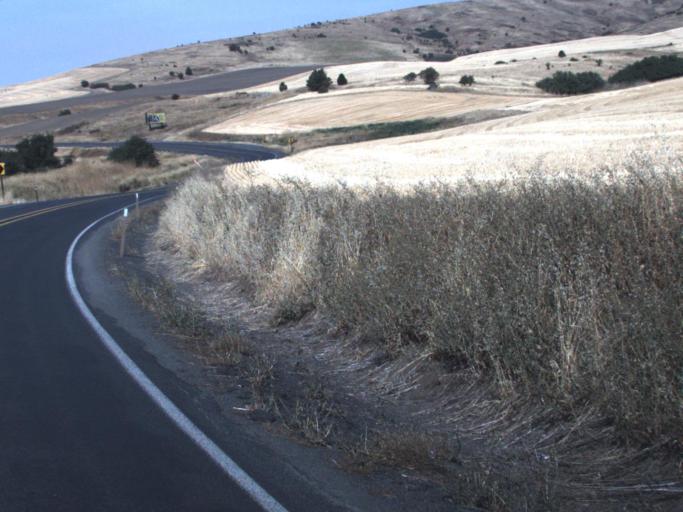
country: US
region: Idaho
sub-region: Benewah County
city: Plummer
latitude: 47.2296
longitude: -117.0943
